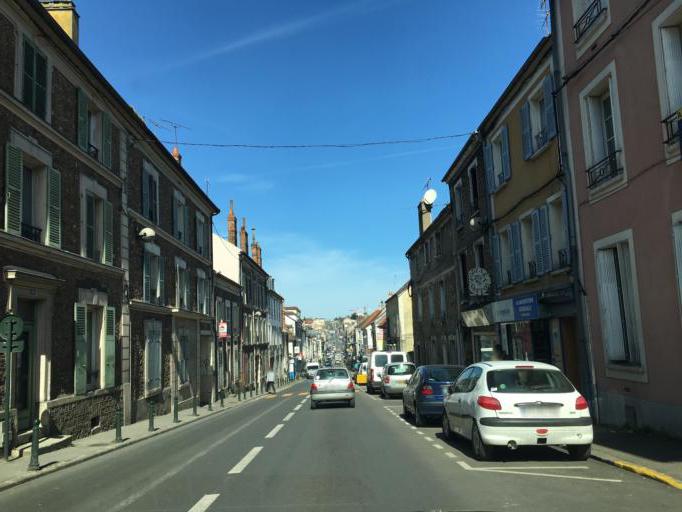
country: FR
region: Ile-de-France
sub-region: Departement de l'Essonne
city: Corbeil-Essonnes
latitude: 48.6015
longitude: 2.4702
